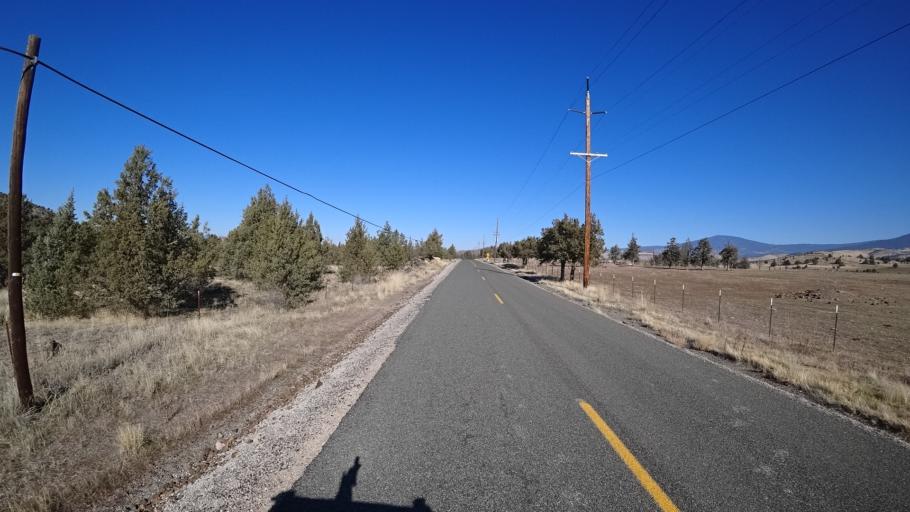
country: US
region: California
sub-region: Siskiyou County
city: Montague
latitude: 41.6688
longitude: -122.3696
